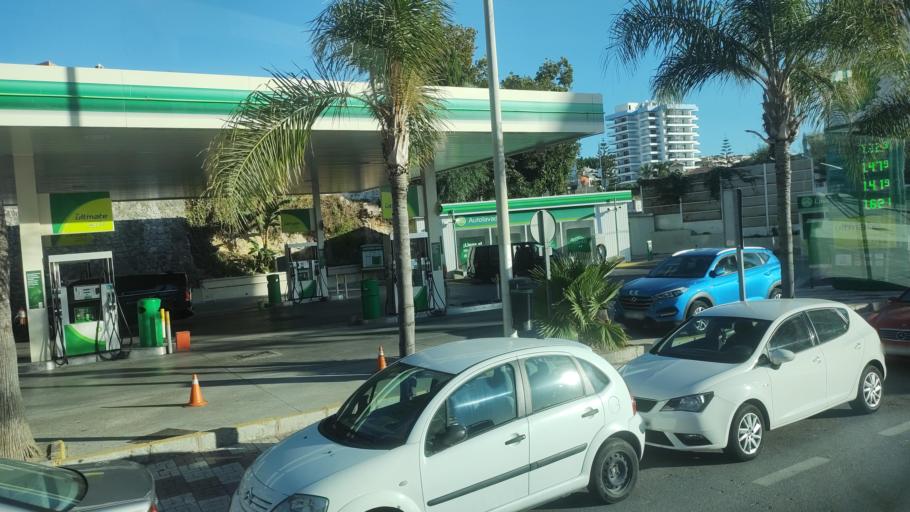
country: ES
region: Andalusia
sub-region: Provincia de Malaga
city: Torremolinos
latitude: 36.6066
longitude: -4.5103
